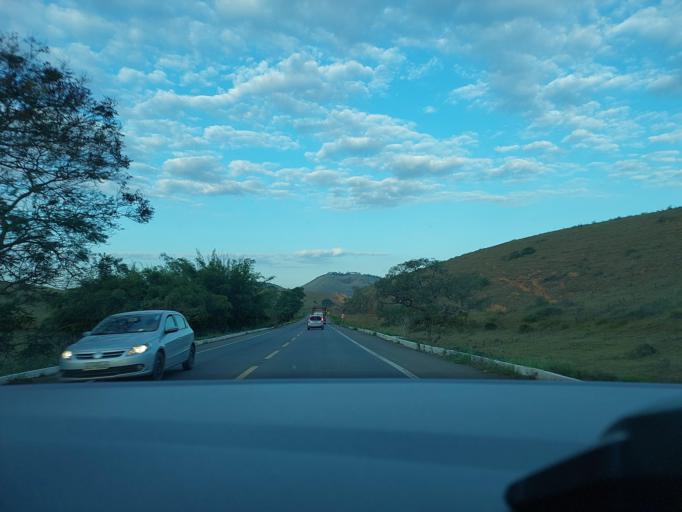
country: BR
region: Rio de Janeiro
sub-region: Natividade
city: Natividade
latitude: -21.1510
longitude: -42.1457
